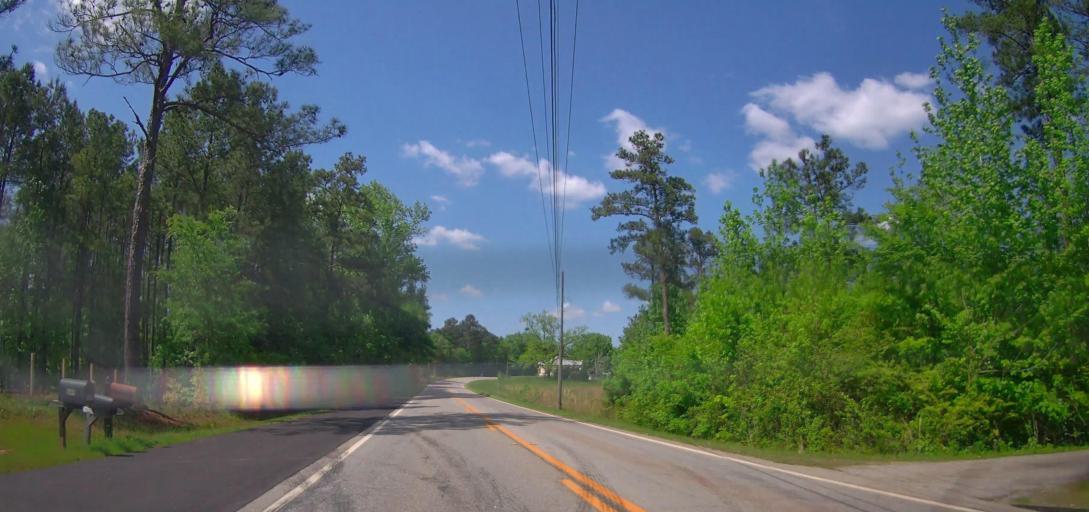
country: US
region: Georgia
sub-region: Putnam County
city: Eatonton
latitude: 33.2798
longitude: -83.3036
